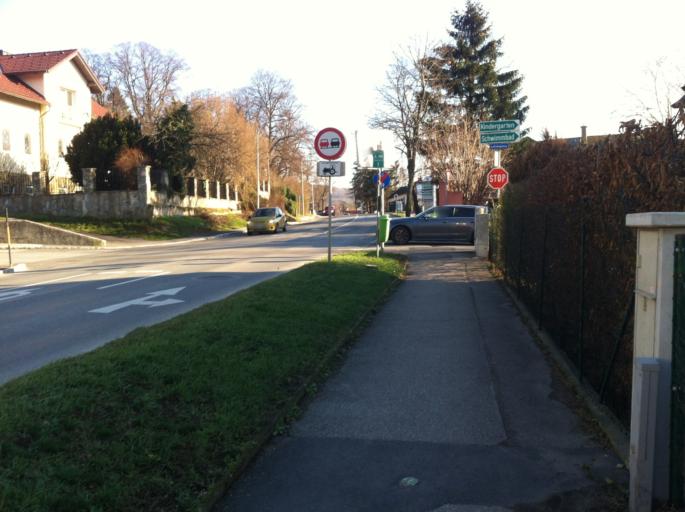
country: AT
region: Lower Austria
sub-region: Politischer Bezirk Wien-Umgebung
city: Gablitz
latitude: 48.2305
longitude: 16.1498
